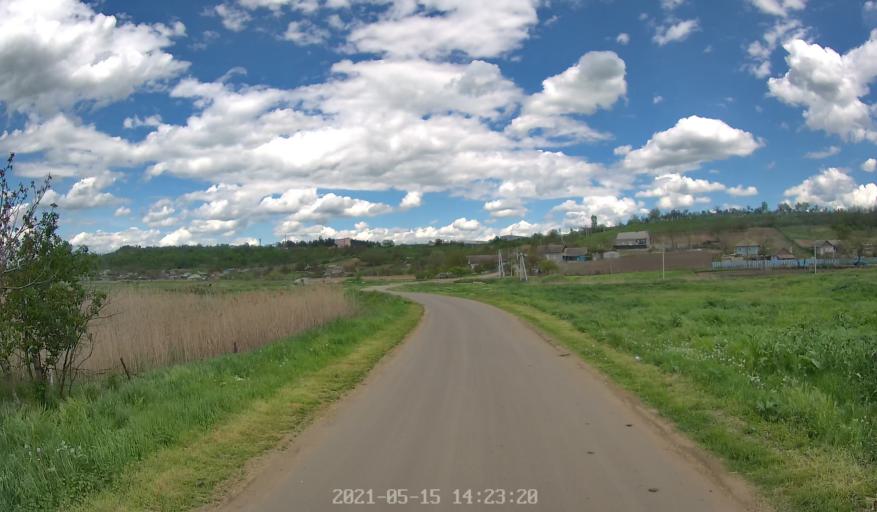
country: MD
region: Hincesti
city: Hincesti
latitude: 46.7376
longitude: 28.5155
